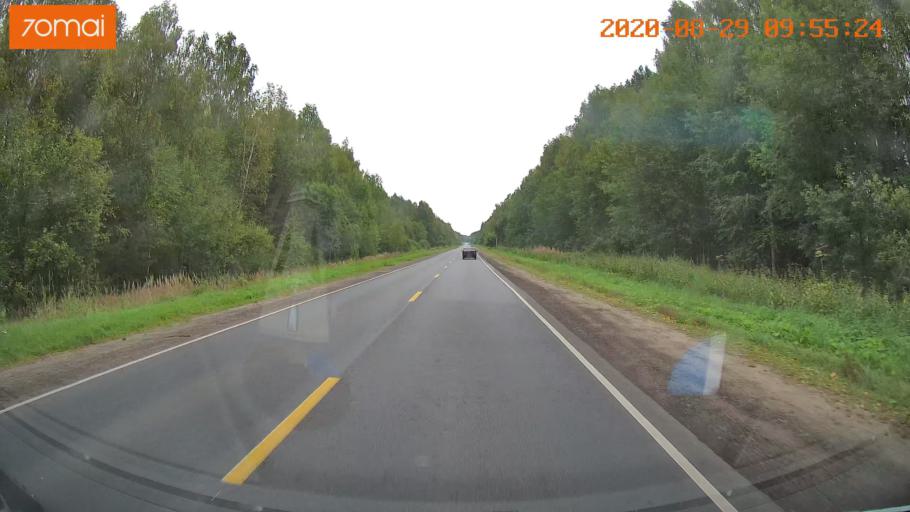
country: RU
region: Ivanovo
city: Zarechnyy
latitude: 57.4223
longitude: 42.2625
